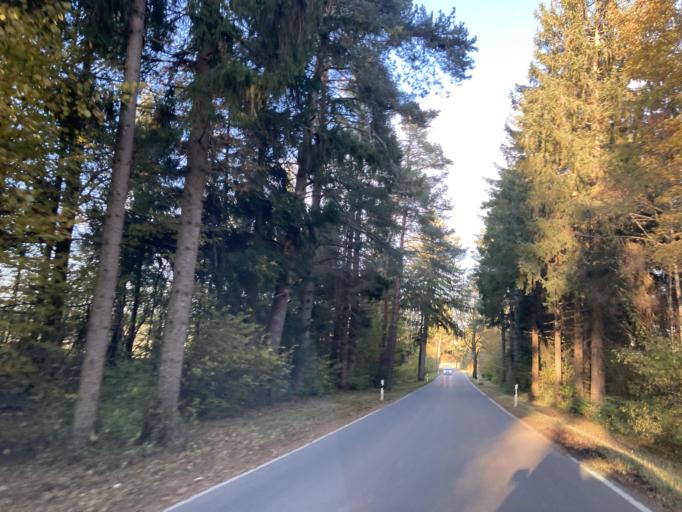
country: DE
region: Baden-Wuerttemberg
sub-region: Freiburg Region
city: Villingen-Schwenningen
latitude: 48.0071
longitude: 8.4409
